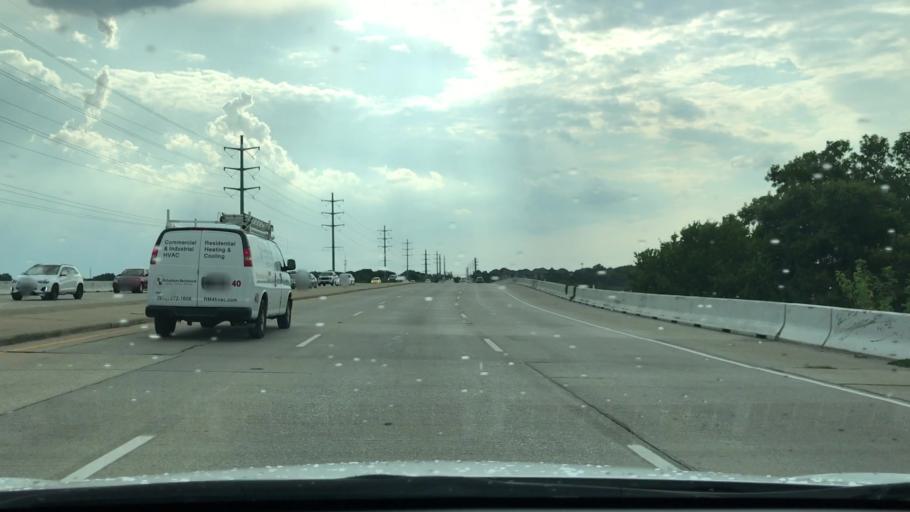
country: US
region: Texas
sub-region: Dallas County
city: Rowlett
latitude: 32.9071
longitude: -96.5372
